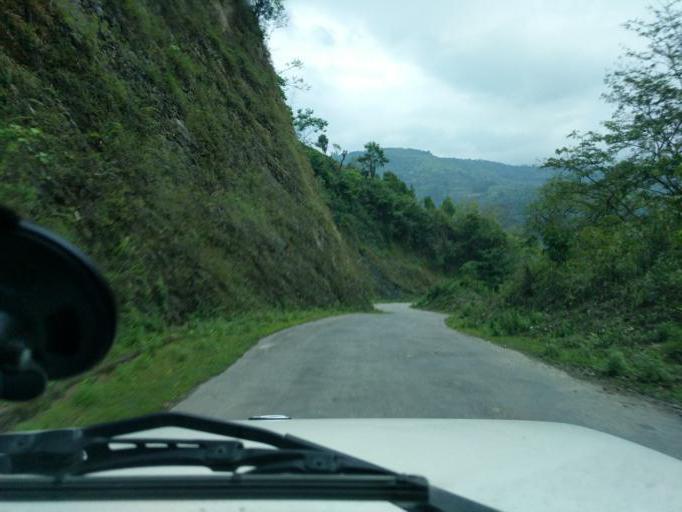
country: BT
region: Mongar
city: Mongar
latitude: 27.2947
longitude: 91.1541
